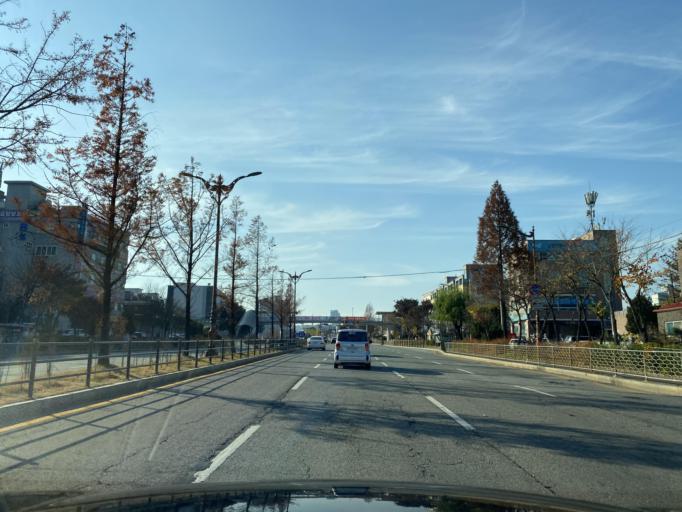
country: KR
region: Chungcheongnam-do
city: Cheonan
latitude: 36.7988
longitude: 127.1373
